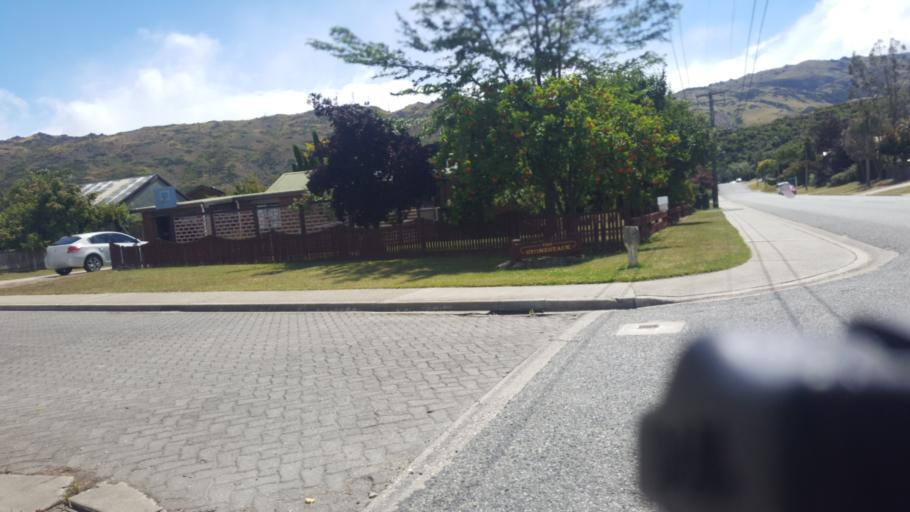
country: NZ
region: Otago
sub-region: Queenstown-Lakes District
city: Wanaka
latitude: -45.1867
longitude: 169.3209
